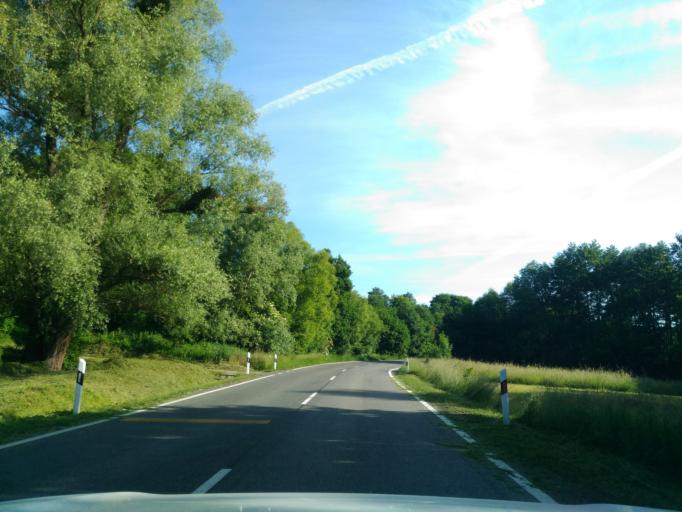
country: HU
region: Baranya
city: Komlo
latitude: 46.1658
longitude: 18.2544
